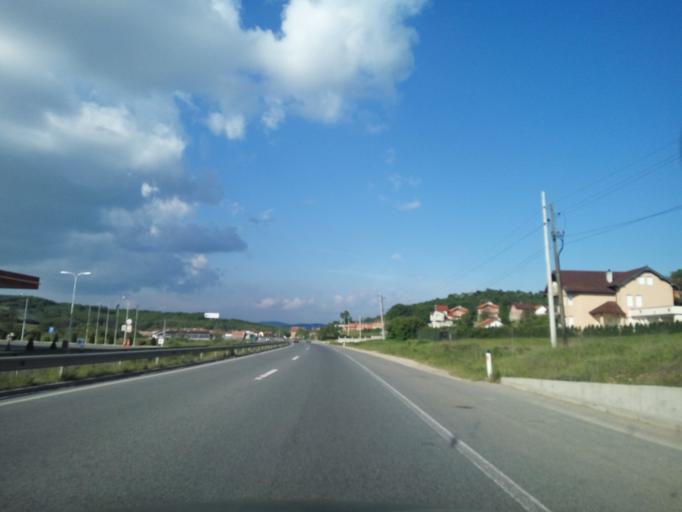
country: XK
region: Pristina
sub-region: Komuna e Drenasit
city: Glogovac
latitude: 42.5724
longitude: 20.8520
